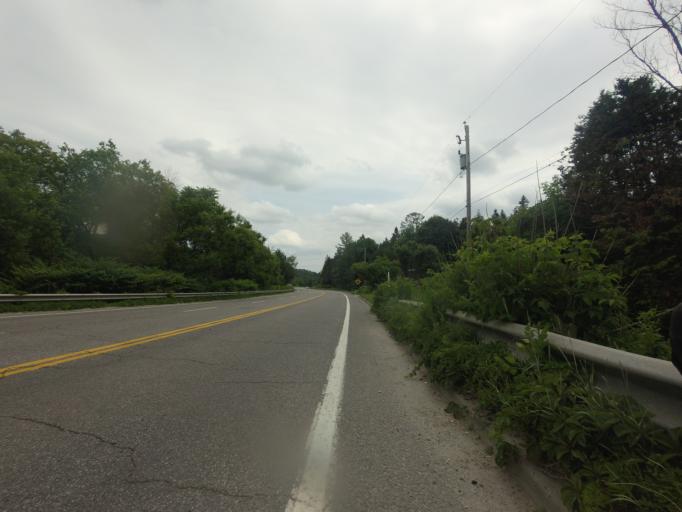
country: CA
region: Quebec
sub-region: Outaouais
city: Wakefield
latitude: 45.7451
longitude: -75.9110
